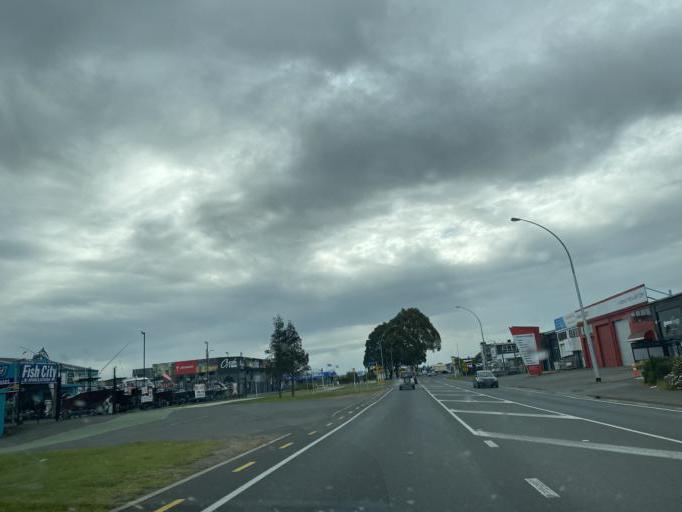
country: NZ
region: Waikato
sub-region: Hamilton City
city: Hamilton
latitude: -37.8058
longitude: 175.2621
